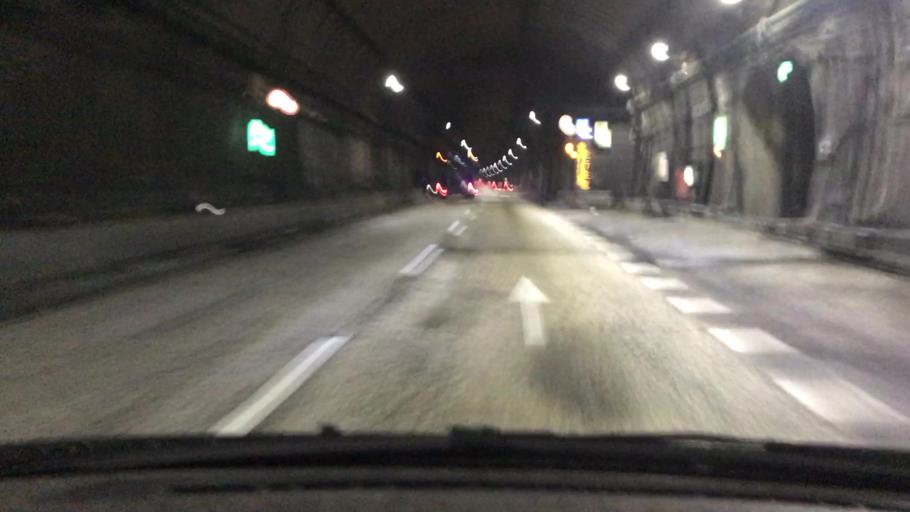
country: JP
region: Hyogo
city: Kobe
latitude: 34.7076
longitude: 135.1944
